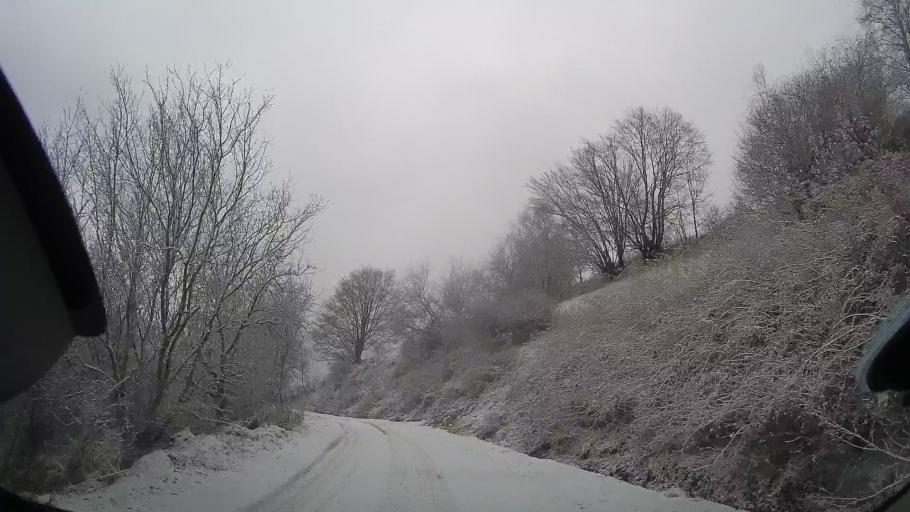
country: RO
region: Cluj
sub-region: Comuna Maguri-Racatau
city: Maguri-Racatau
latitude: 46.6632
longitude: 23.1875
